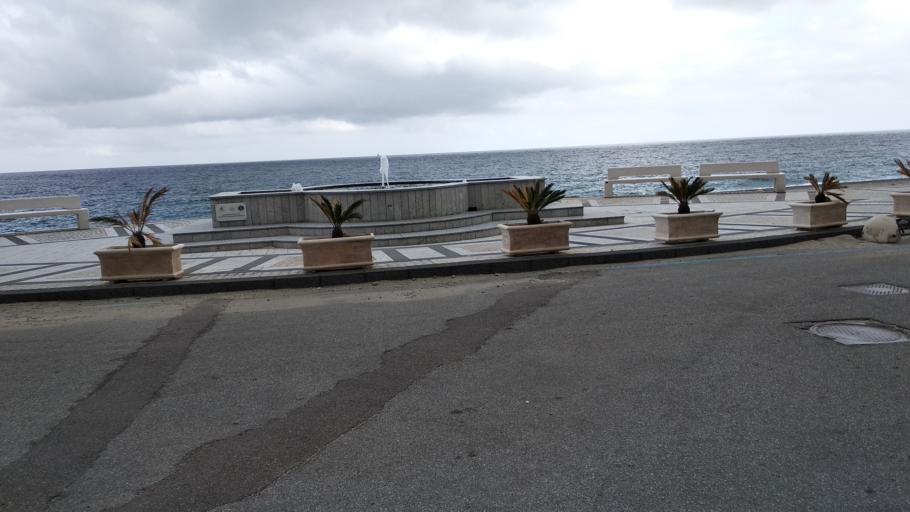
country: IT
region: Calabria
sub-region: Provincia di Reggio Calabria
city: Scilla
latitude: 38.2520
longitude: 15.7108
